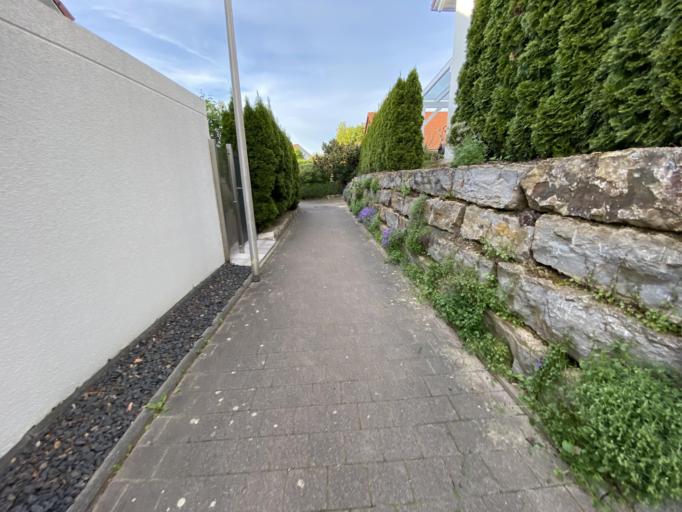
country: DE
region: Baden-Wuerttemberg
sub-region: Regierungsbezirk Stuttgart
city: Leingarten
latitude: 49.1418
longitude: 9.1036
